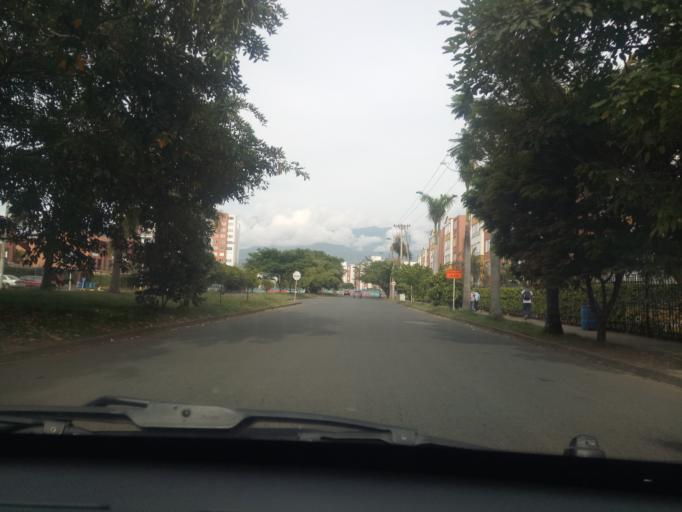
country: CO
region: Valle del Cauca
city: Cali
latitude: 3.3685
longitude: -76.5190
